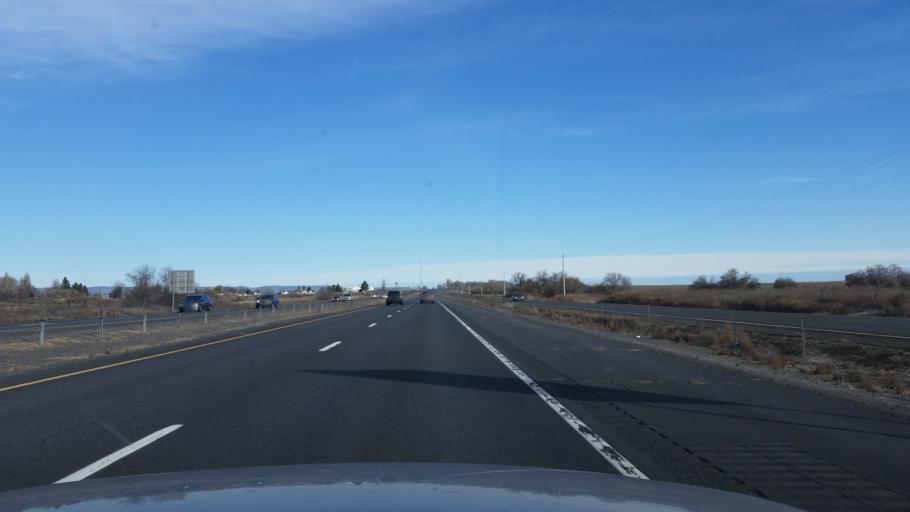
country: US
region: Washington
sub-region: Grant County
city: Quincy
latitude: 47.0949
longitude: -119.8435
